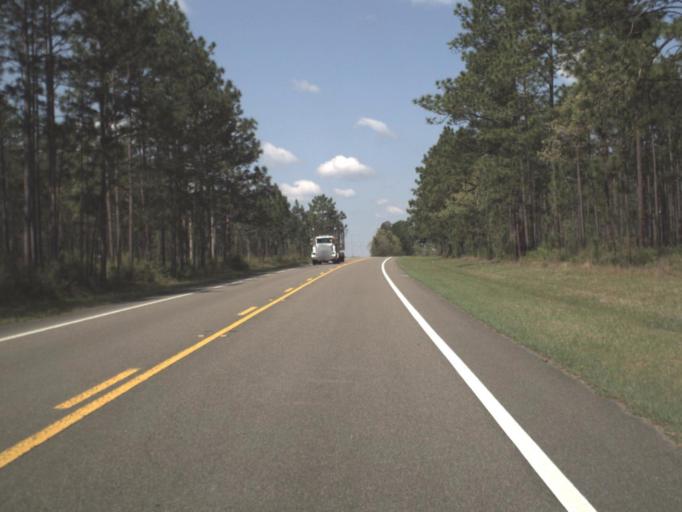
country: US
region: Florida
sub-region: Okaloosa County
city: Crestview
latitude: 30.8509
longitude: -86.8035
